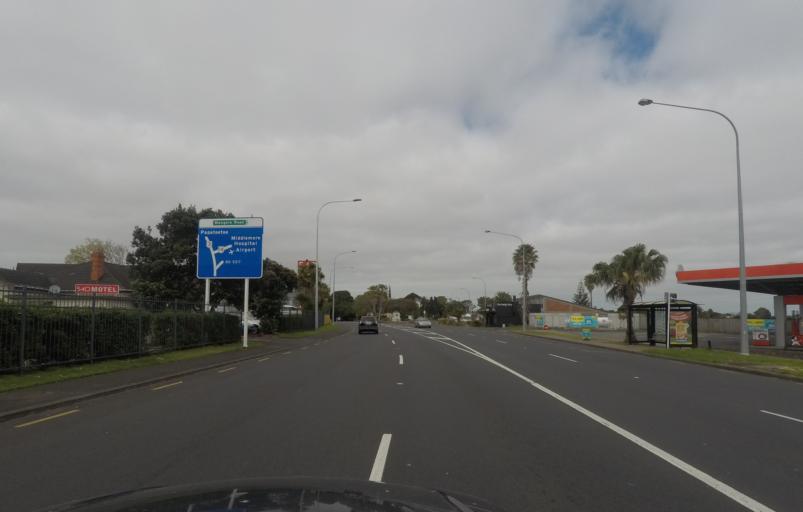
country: NZ
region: Auckland
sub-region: Auckland
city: Mangere
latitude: -36.9489
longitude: 174.8456
